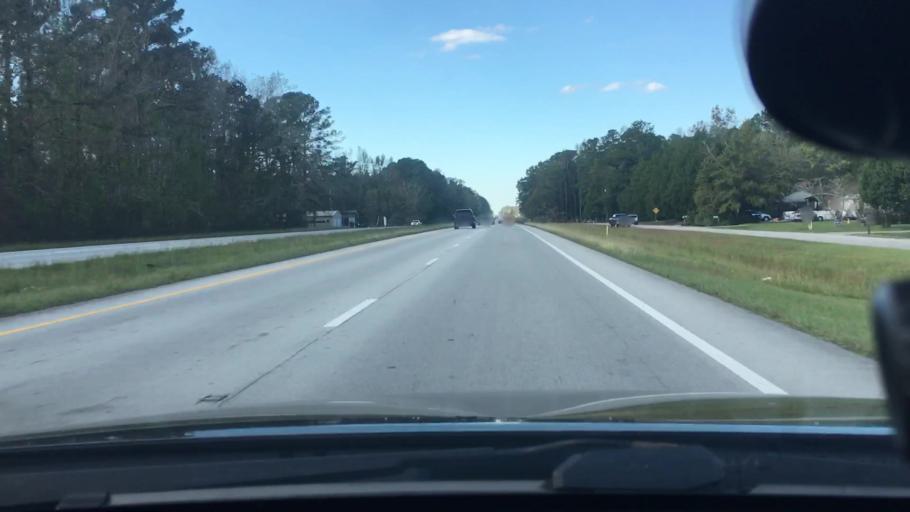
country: US
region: North Carolina
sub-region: Craven County
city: Fairfield Harbour
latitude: 35.0226
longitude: -76.9987
